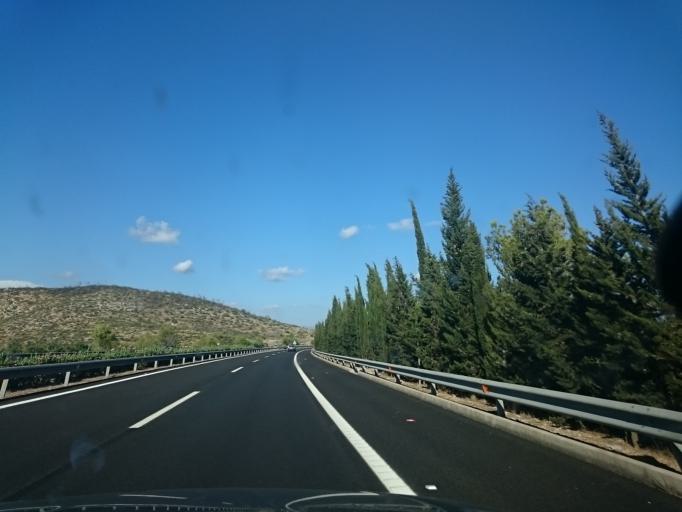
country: ES
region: Catalonia
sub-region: Provincia de Barcelona
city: Vilanova i la Geltru
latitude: 41.2488
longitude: 1.6991
